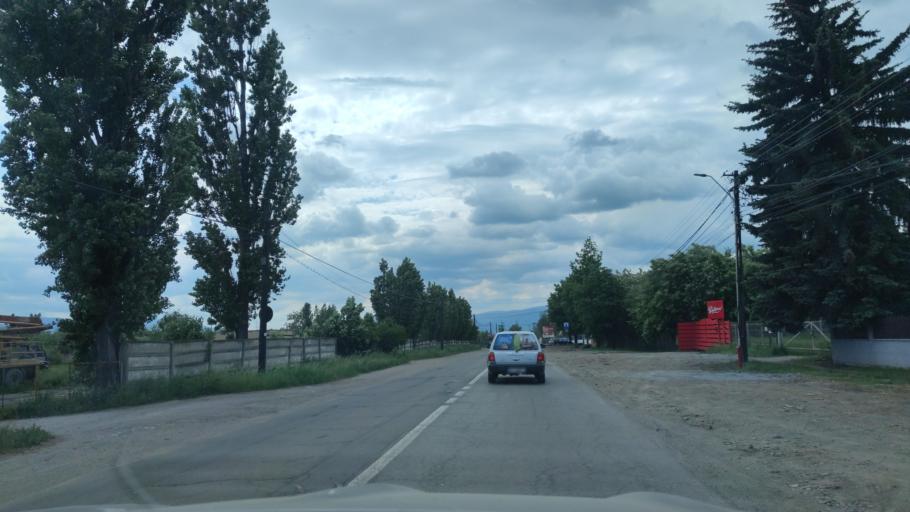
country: RO
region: Harghita
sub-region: Municipiul Gheorgheni
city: Gheorgheni
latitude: 46.7136
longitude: 25.5702
